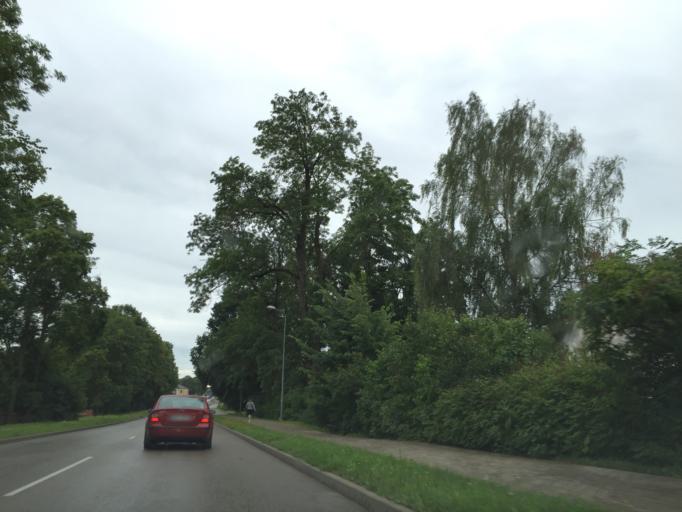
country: LV
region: Jekabpils Rajons
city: Jekabpils
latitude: 56.5092
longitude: 25.8604
